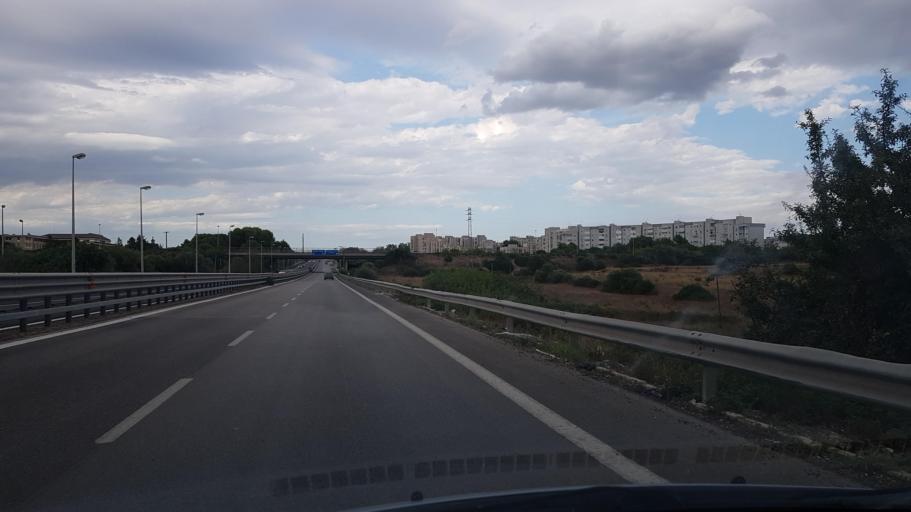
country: IT
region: Apulia
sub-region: Provincia di Taranto
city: Paolo VI
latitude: 40.5149
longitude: 17.2536
